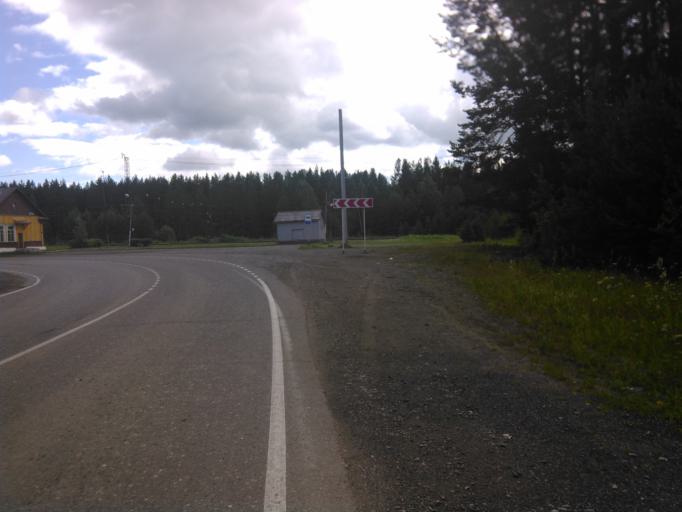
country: RU
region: Sverdlovsk
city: Krasnotur'insk
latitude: 59.7333
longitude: 60.2033
